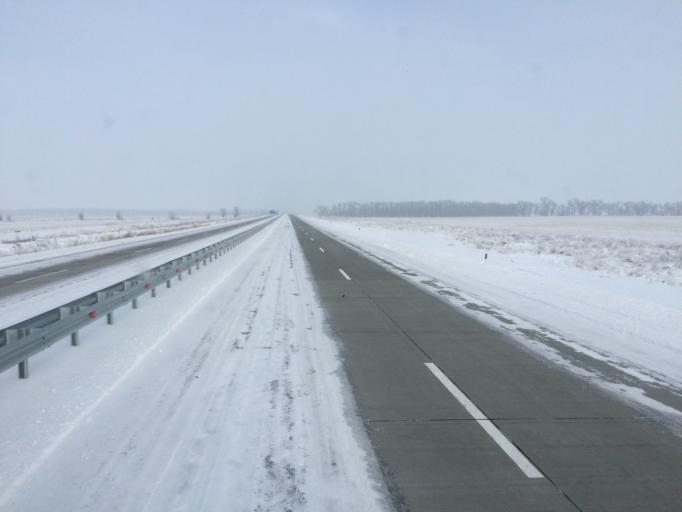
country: KG
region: Chuy
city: Sokuluk
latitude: 43.2980
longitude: 74.2499
